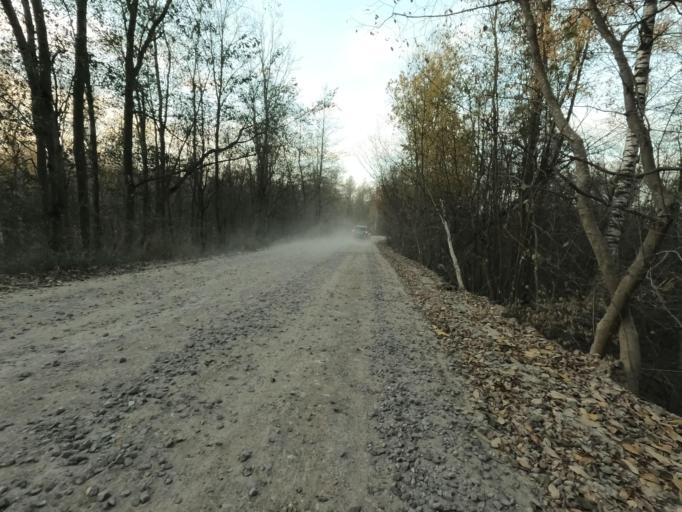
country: RU
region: Leningrad
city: Mga
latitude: 59.7719
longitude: 31.2269
